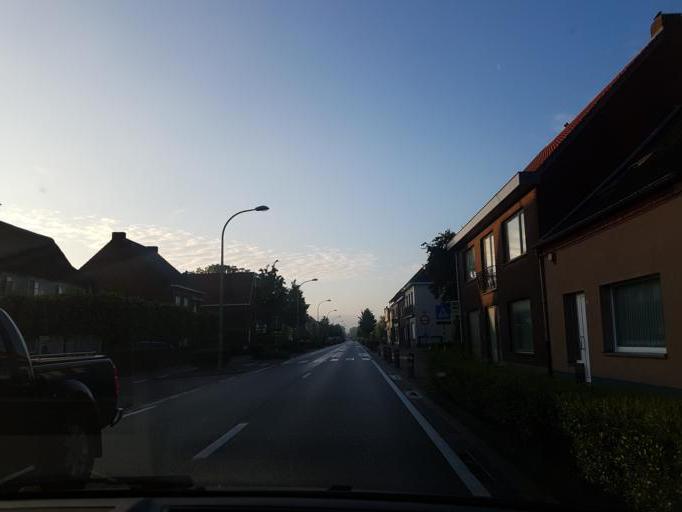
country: BE
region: Flanders
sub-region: Provincie Antwerpen
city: Hoogstraten
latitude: 51.3961
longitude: 4.7978
